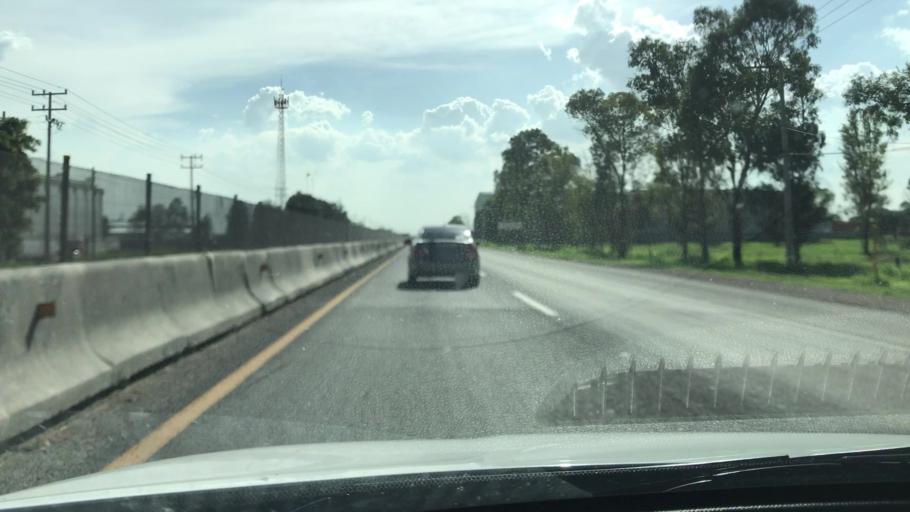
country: MX
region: Guanajuato
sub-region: Cortazar
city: Colonia la Calzada (La Olla)
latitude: 20.5101
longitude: -100.9689
